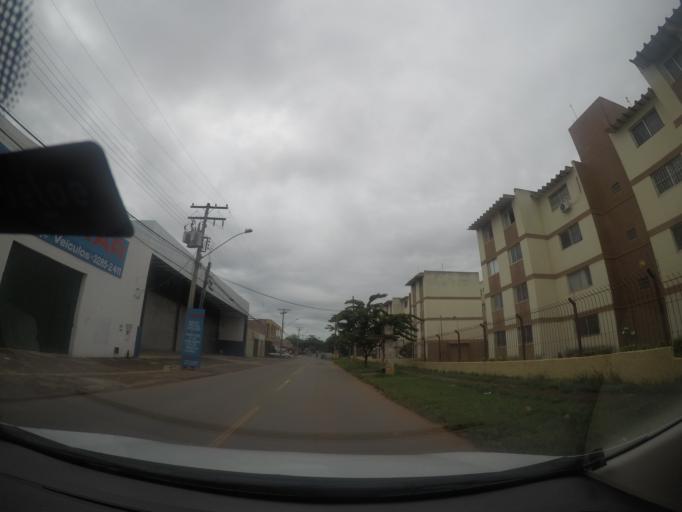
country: BR
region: Goias
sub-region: Goiania
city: Goiania
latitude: -16.6965
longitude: -49.3245
